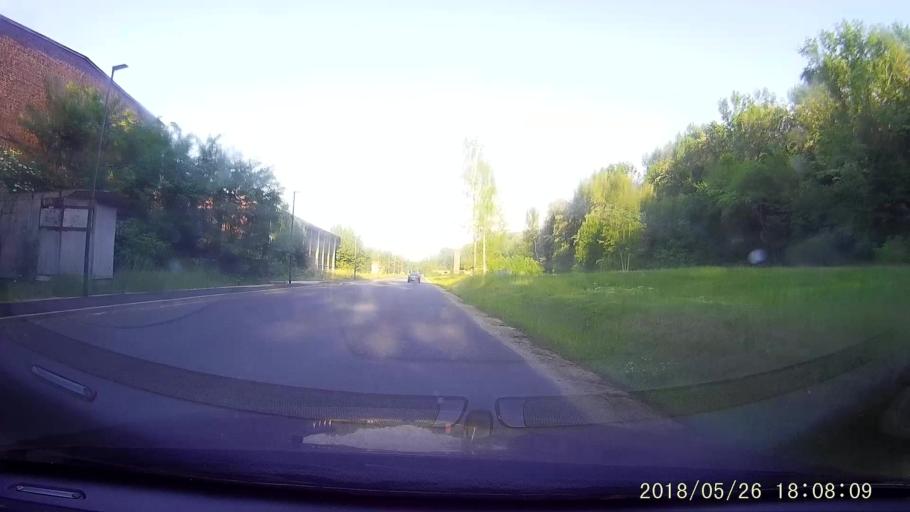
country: DE
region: Saxony
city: Schonau-Berzdorf
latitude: 51.0676
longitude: 14.9329
